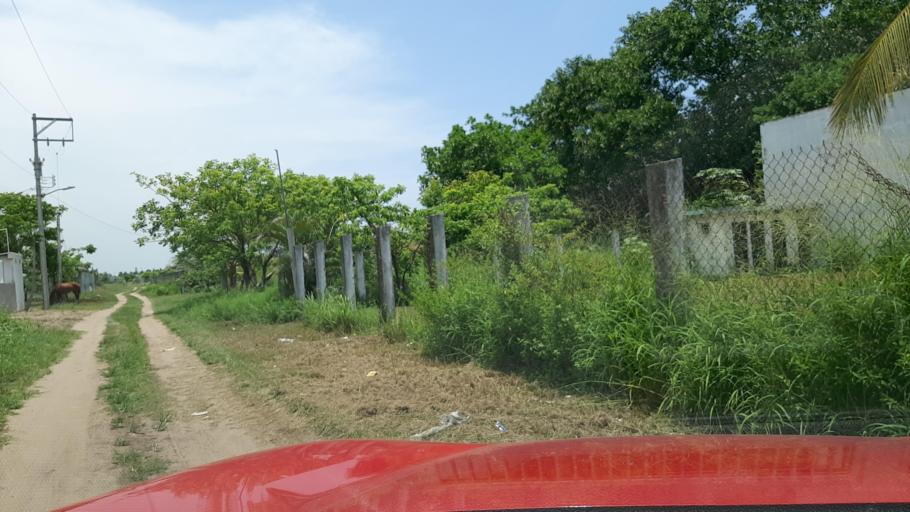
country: MX
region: Veracruz
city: San Rafael
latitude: 20.2939
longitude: -96.8406
